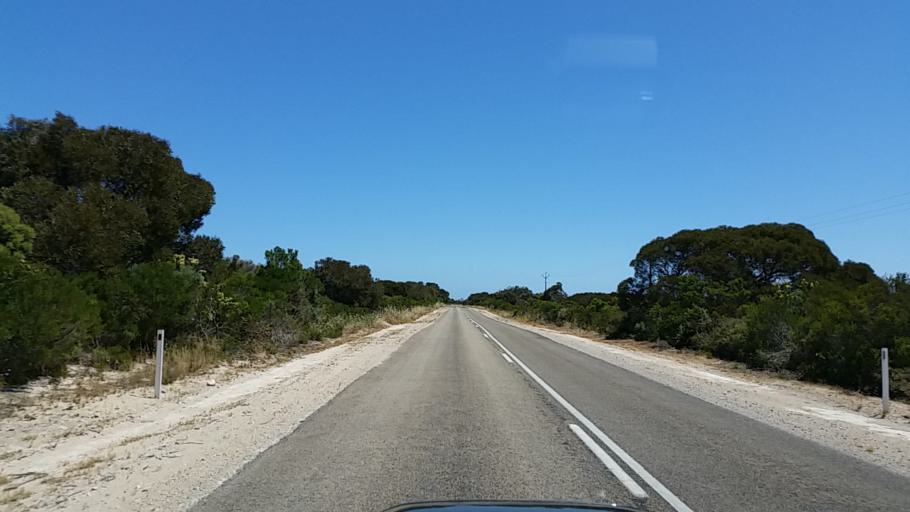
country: AU
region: South Australia
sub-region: Yorke Peninsula
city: Honiton
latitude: -35.2176
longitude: 137.0012
